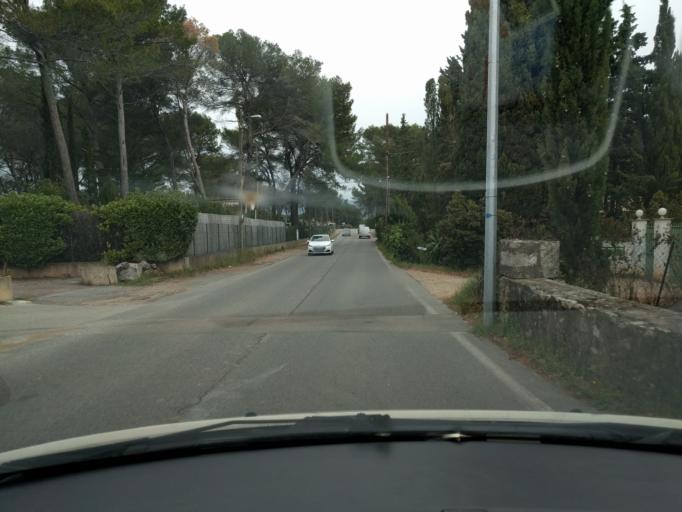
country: FR
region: Provence-Alpes-Cote d'Azur
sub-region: Departement des Alpes-Maritimes
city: La Roquette-sur-Siagne
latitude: 43.6021
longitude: 6.9591
